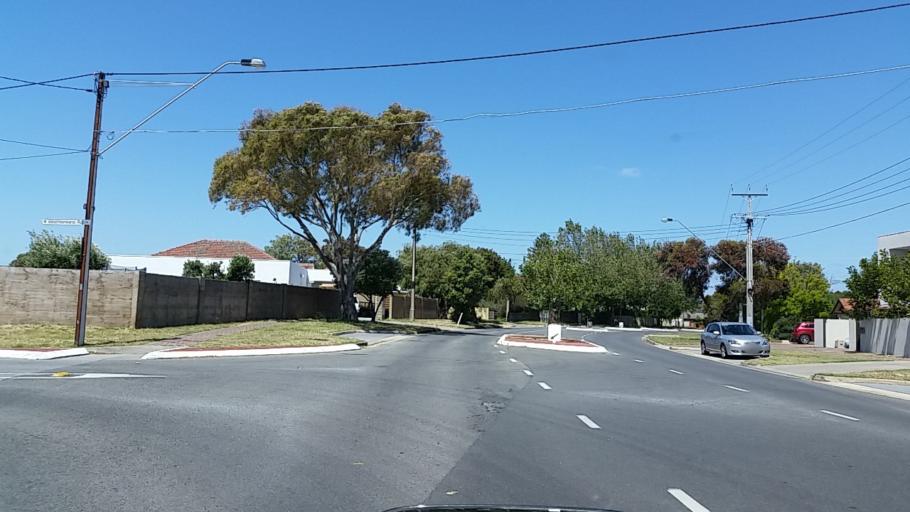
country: AU
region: South Australia
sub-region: Charles Sturt
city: Grange
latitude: -34.9046
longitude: 138.5006
